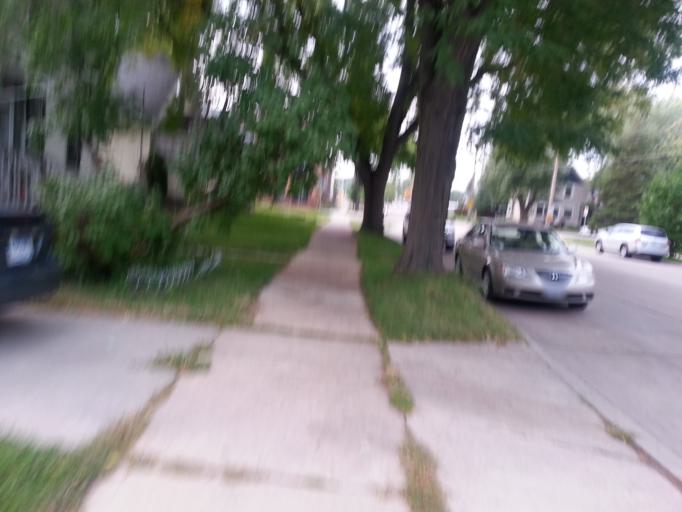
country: US
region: Minnesota
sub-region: Olmsted County
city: Rochester
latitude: 44.0267
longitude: -92.4711
